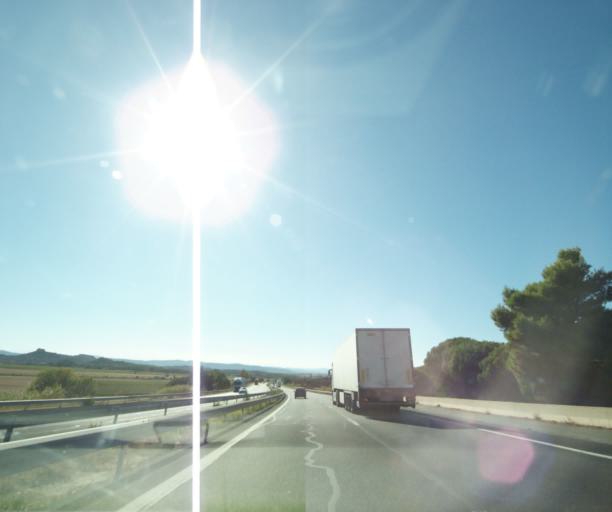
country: FR
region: Languedoc-Roussillon
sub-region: Departement de l'Aude
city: Bizanet
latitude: 43.1551
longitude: 2.8885
